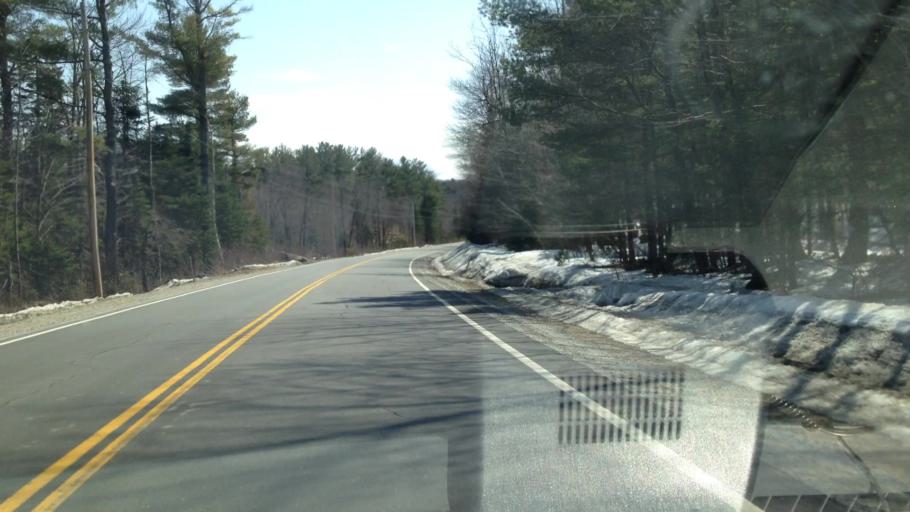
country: US
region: New Hampshire
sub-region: Merrimack County
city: Wilmot
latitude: 43.4785
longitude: -71.9696
